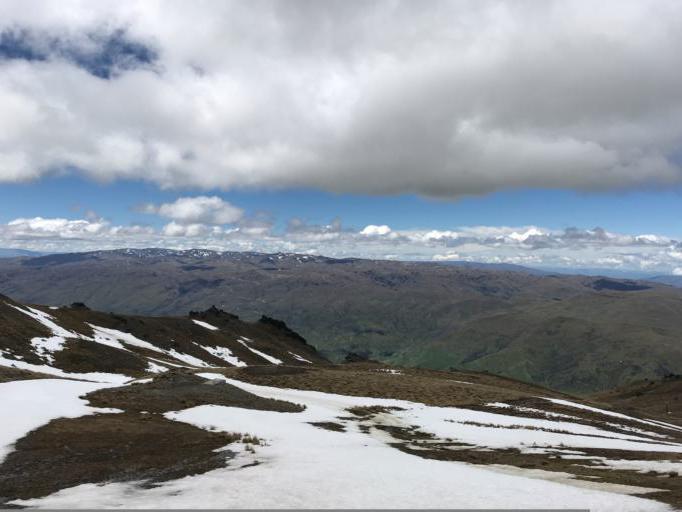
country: NZ
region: Otago
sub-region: Queenstown-Lakes District
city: Arrowtown
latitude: -44.8572
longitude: 168.9468
